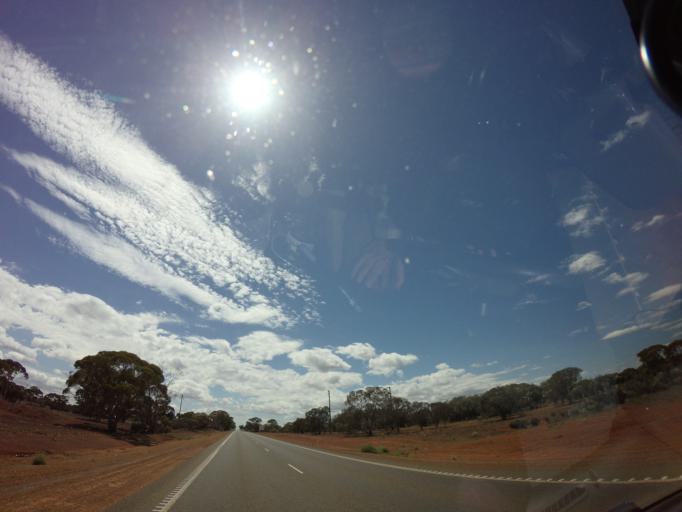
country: AU
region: Western Australia
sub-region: Kalgoorlie/Boulder
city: Boulder
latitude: -30.9546
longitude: 121.1508
